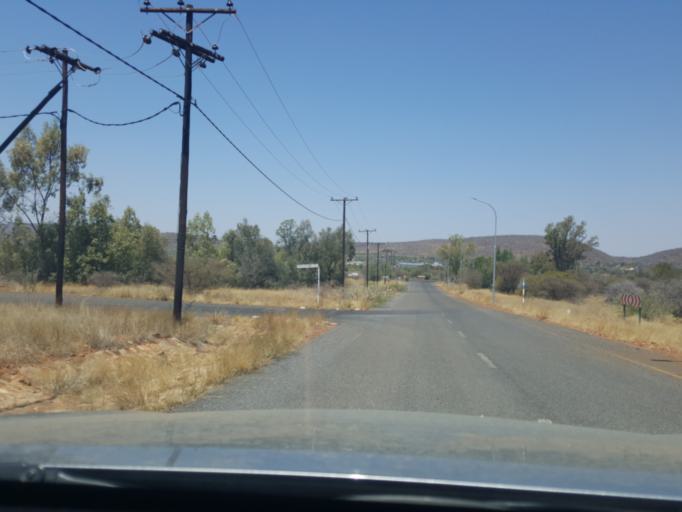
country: BW
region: South East
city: Lobatse
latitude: -25.1900
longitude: 25.6761
